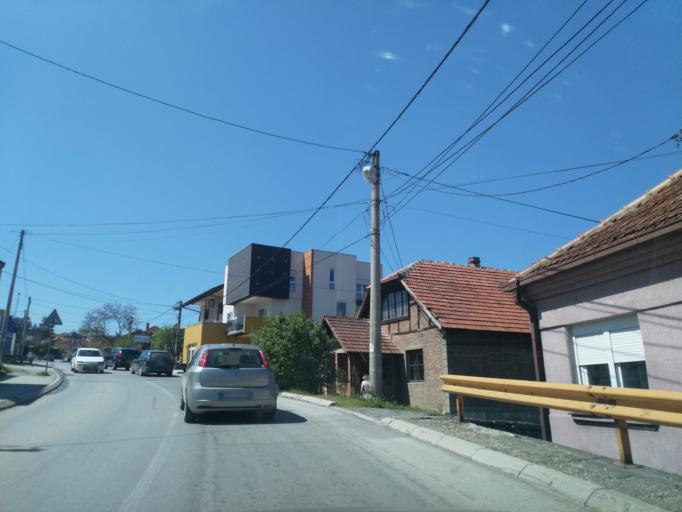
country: RS
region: Central Serbia
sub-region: Kolubarski Okrug
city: Valjevo
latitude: 44.2769
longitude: 19.8762
